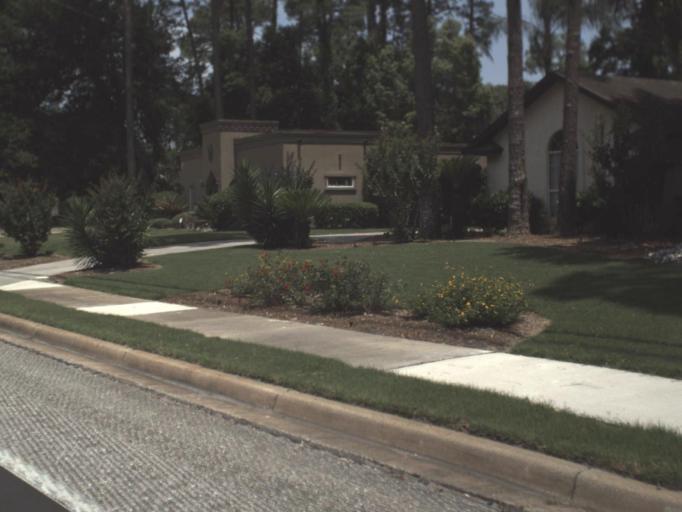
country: US
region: Florida
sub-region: Duval County
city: Jacksonville
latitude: 30.2490
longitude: -81.6366
